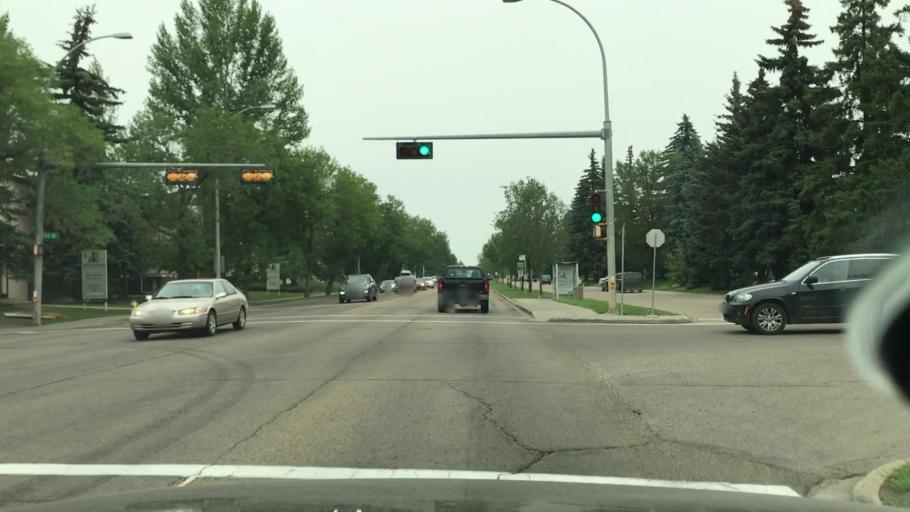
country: CA
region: Alberta
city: Edmonton
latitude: 53.5247
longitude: -113.5779
